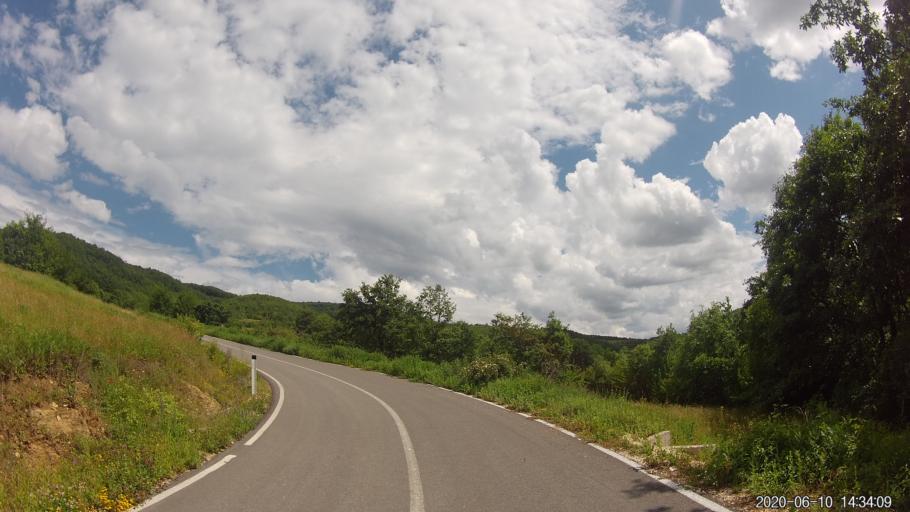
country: XK
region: Prizren
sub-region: Komuna e Therandes
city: Budakovo
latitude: 42.4158
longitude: 20.9295
